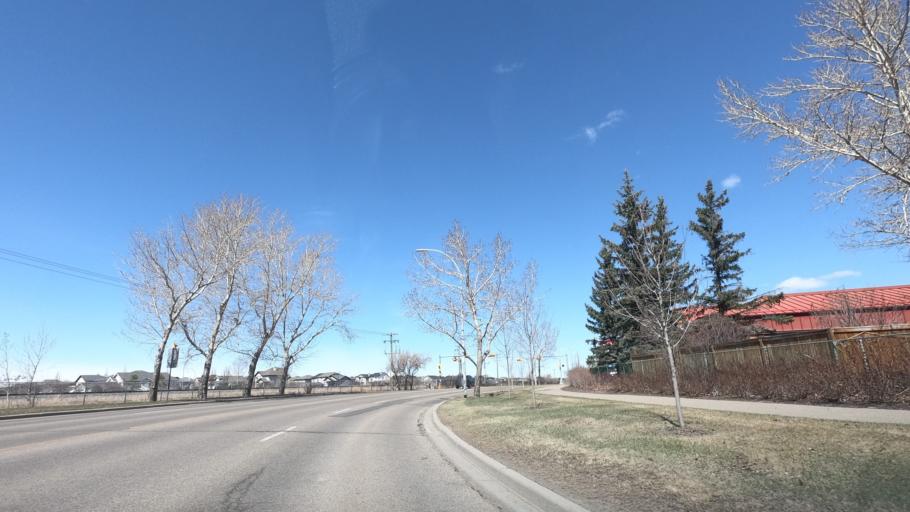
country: CA
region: Alberta
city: Airdrie
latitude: 51.2729
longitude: -114.0121
